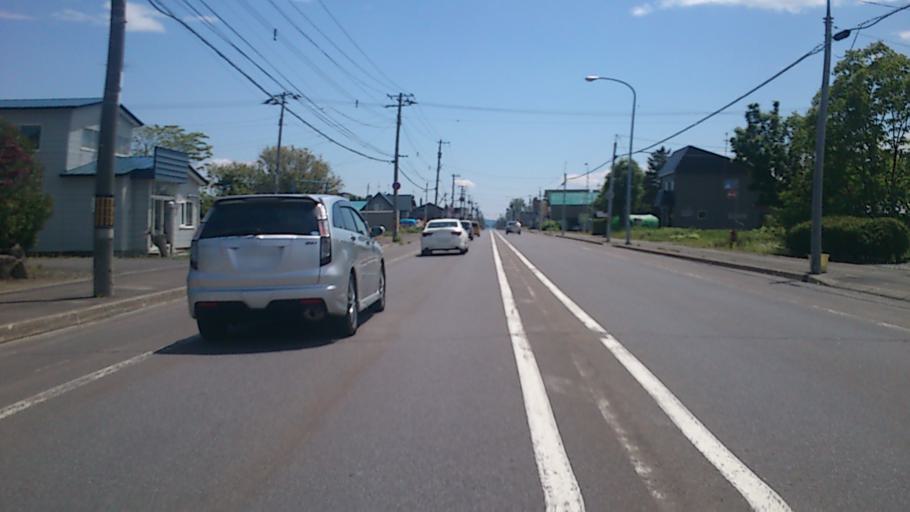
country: JP
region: Hokkaido
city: Nayoro
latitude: 44.2448
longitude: 142.3950
